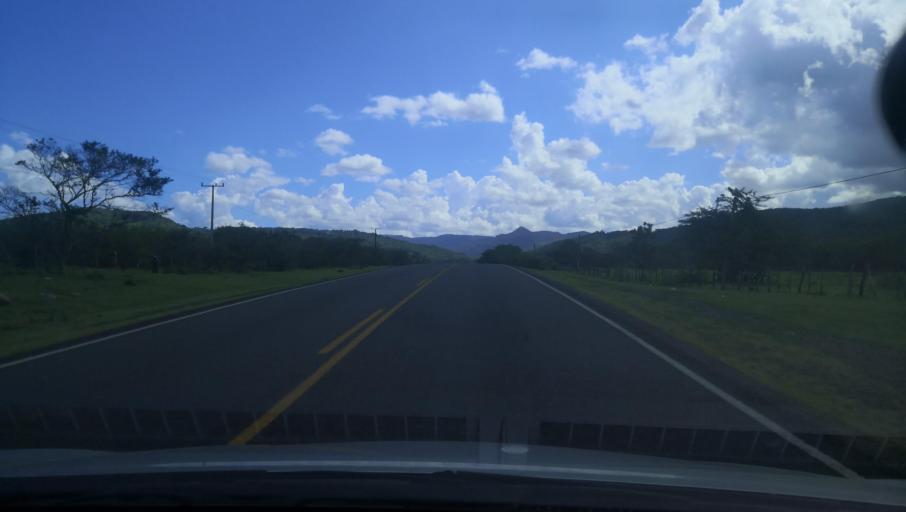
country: NI
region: Madriz
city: Somoto
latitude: 13.4624
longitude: -86.6610
